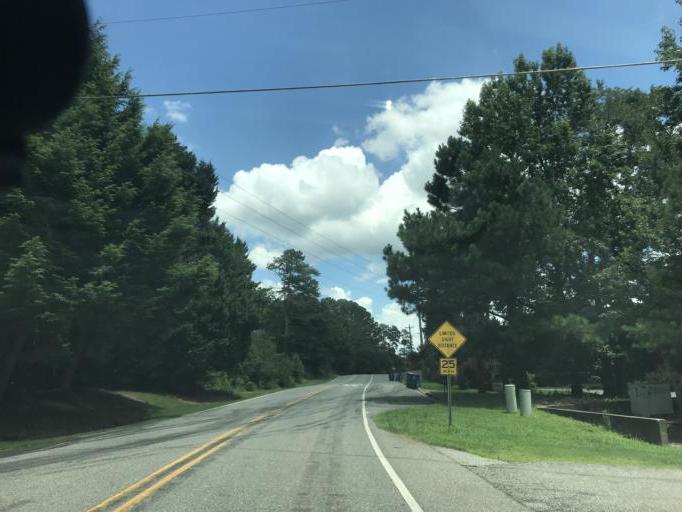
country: US
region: Georgia
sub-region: Fulton County
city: Johns Creek
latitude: 34.1090
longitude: -84.1659
